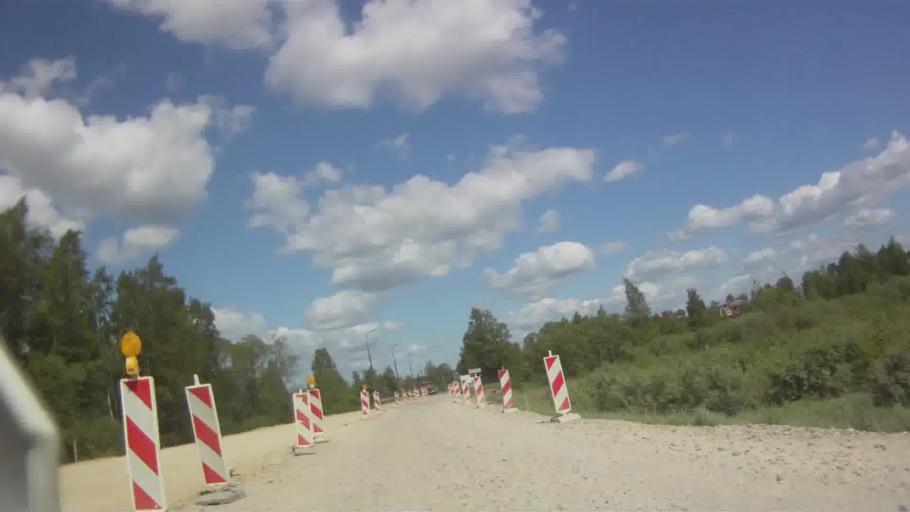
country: LV
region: Rezekne
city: Rezekne
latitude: 56.4907
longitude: 27.3151
